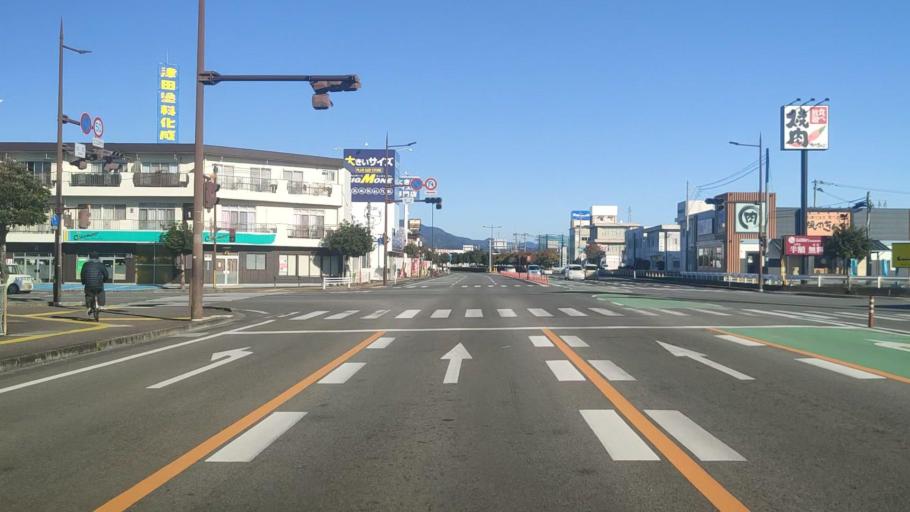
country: JP
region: Miyazaki
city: Nobeoka
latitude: 32.5755
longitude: 131.6835
